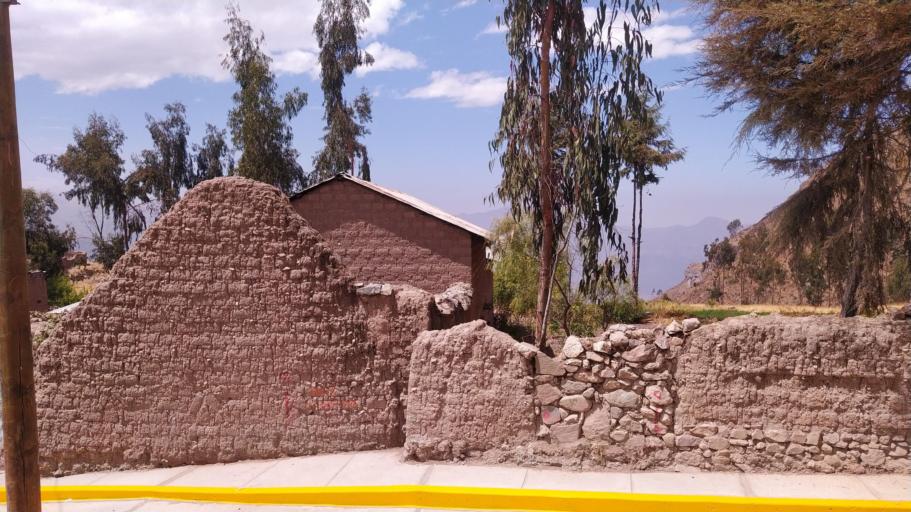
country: PE
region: Lima
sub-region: Provincia de Huarochiri
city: Cocachacra
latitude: -12.0007
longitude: -76.4761
